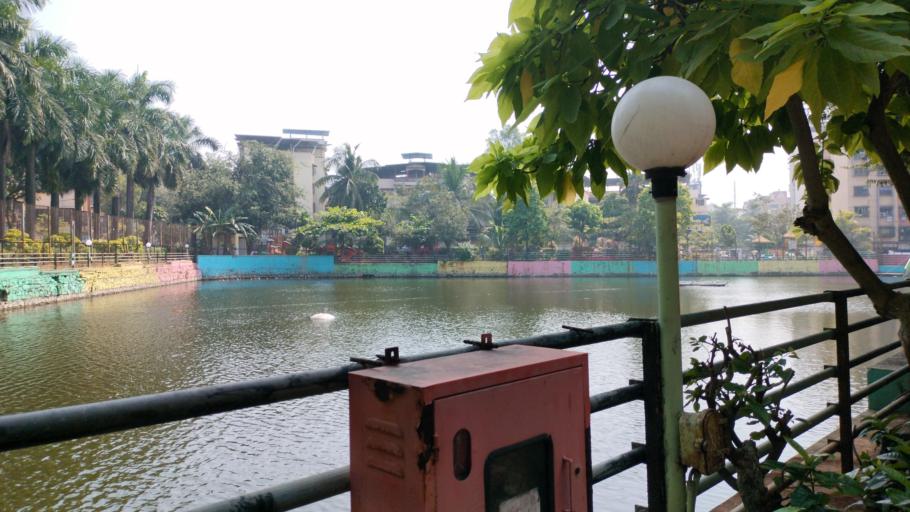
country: IN
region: Maharashtra
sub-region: Thane
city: Bhayandar
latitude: 19.2995
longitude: 72.8493
